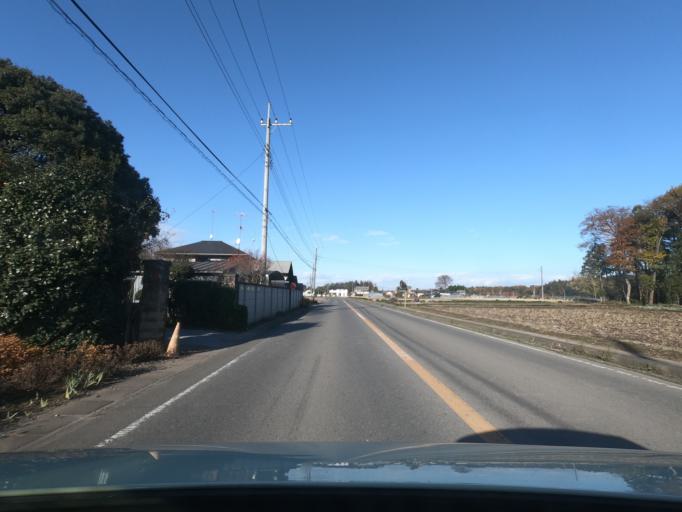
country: JP
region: Ibaraki
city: Koga
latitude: 36.2187
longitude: 139.7698
